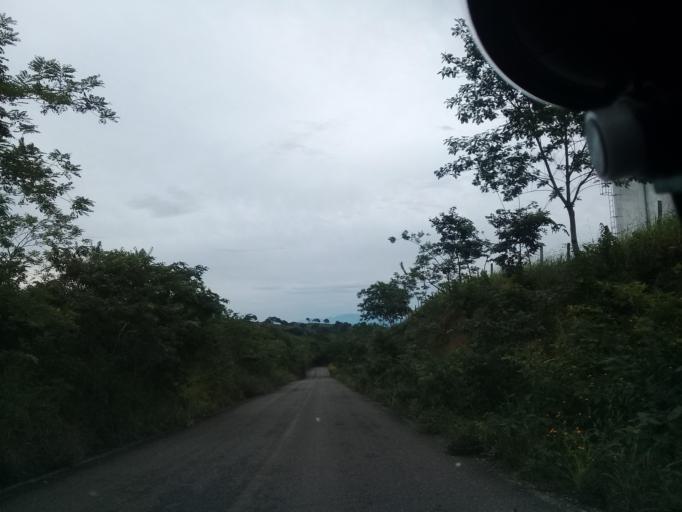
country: MX
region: Hidalgo
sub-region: Huejutla de Reyes
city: Chalahuiyapa
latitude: 21.1999
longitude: -98.3419
